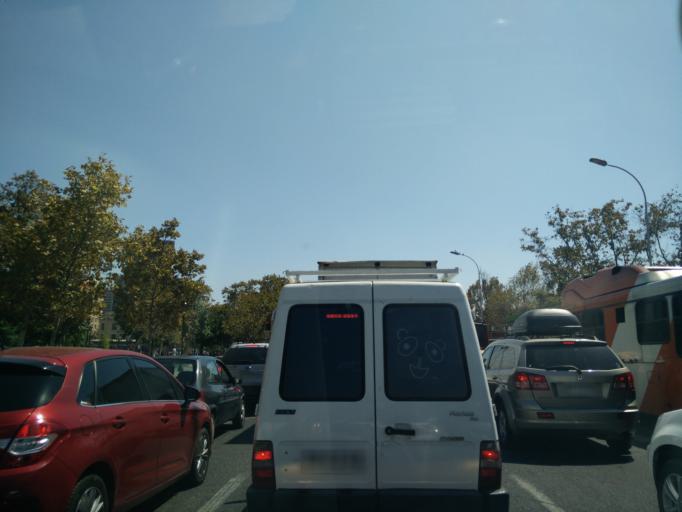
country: CL
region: Santiago Metropolitan
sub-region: Provincia de Santiago
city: Santiago
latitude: -33.4330
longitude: -70.6499
